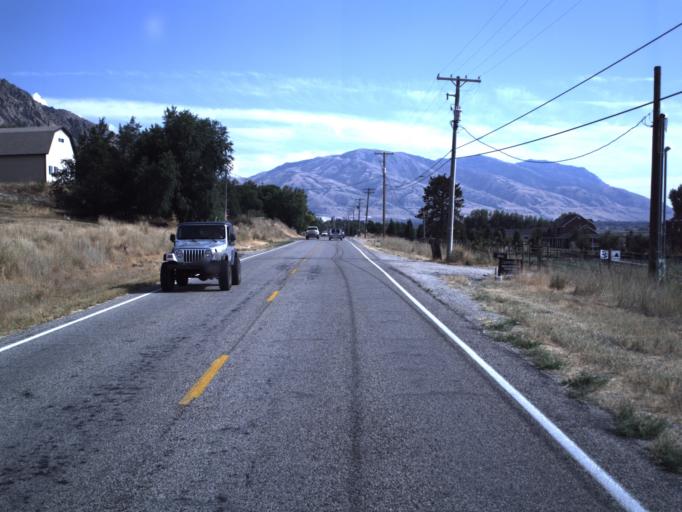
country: US
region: Utah
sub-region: Box Elder County
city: Brigham City
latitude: 41.5739
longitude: -112.0310
